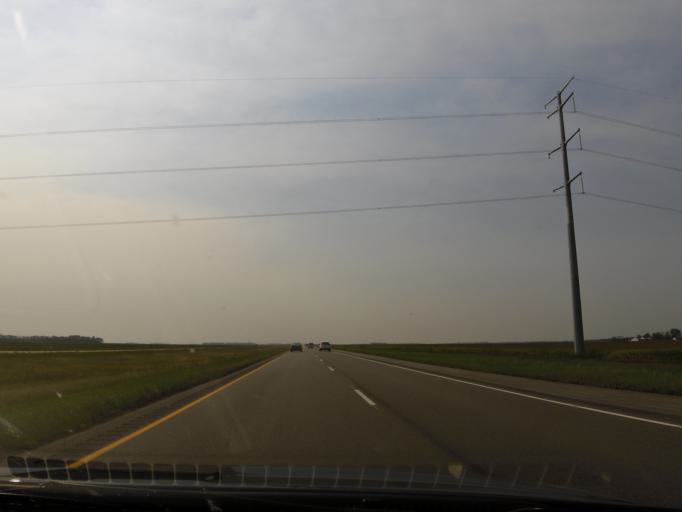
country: US
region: North Dakota
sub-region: Cass County
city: Horace
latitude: 46.6857
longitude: -96.8311
